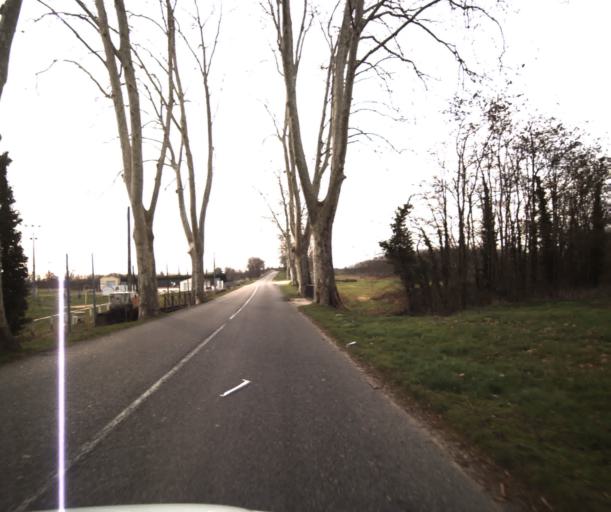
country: FR
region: Midi-Pyrenees
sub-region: Departement du Tarn-et-Garonne
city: Campsas
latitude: 43.8984
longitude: 1.3202
